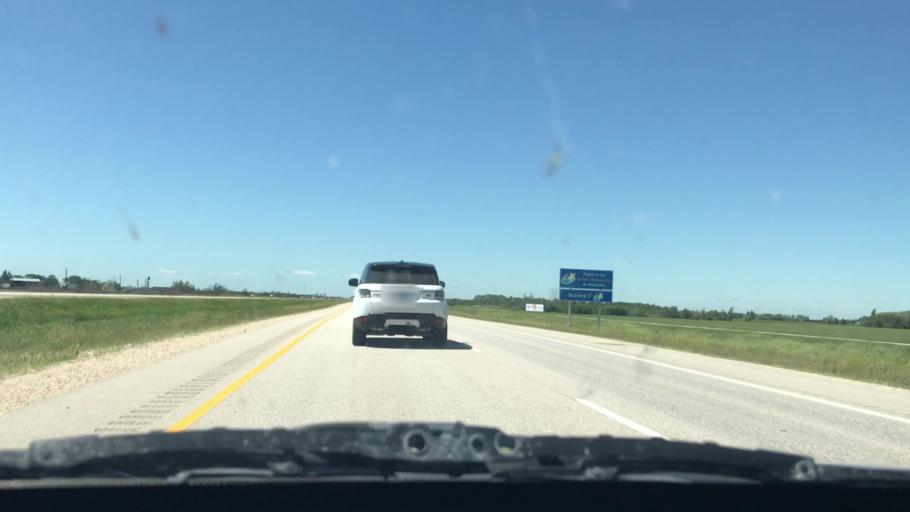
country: CA
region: Manitoba
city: Niverville
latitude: 49.8043
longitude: -96.8970
